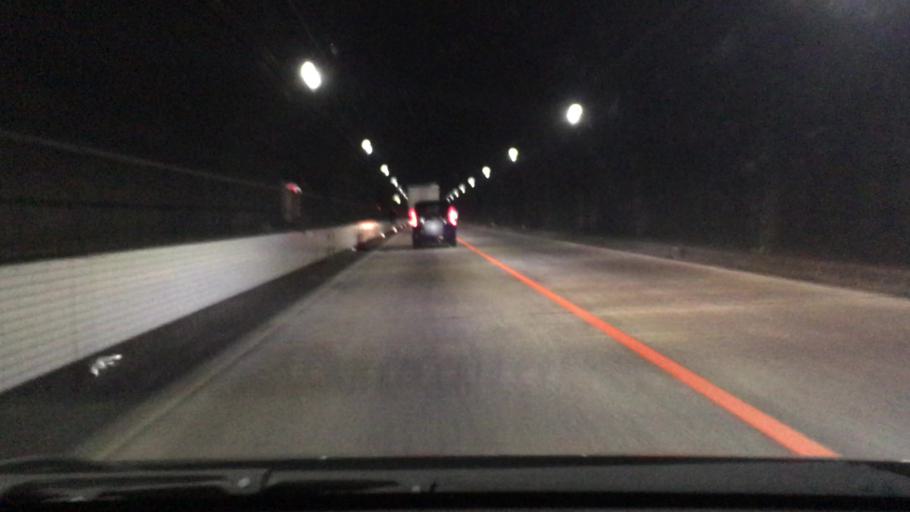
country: JP
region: Yamaguchi
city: Otake
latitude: 34.2147
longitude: 132.1921
